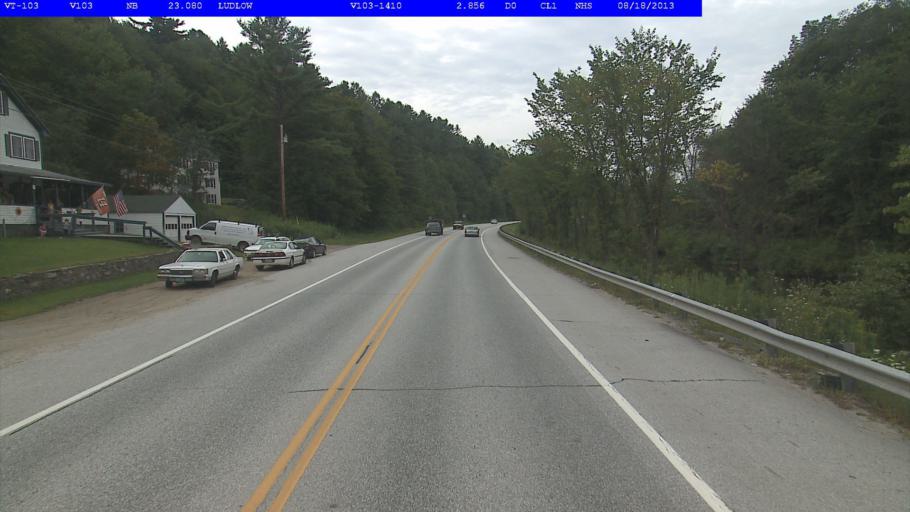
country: US
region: Vermont
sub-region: Windsor County
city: Chester
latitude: 43.4034
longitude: -72.7075
